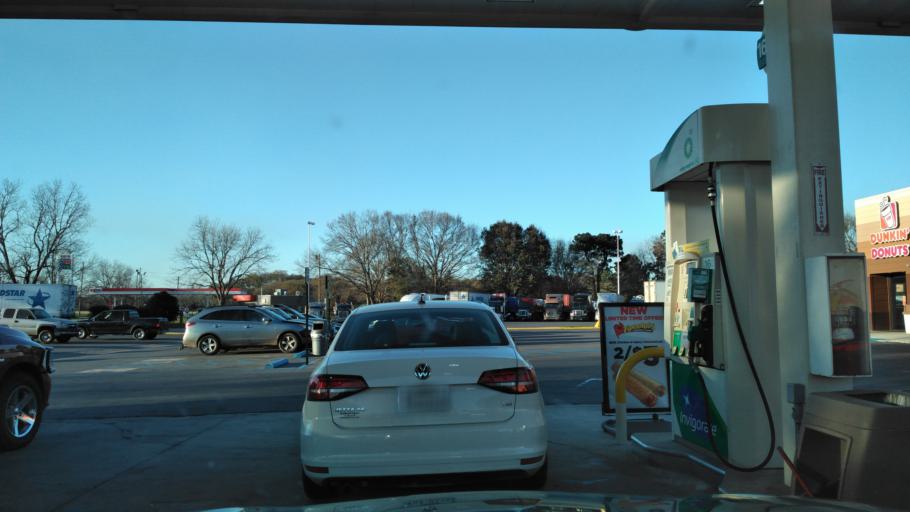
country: US
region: Alabama
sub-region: Mobile County
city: Grand Bay
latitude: 30.4984
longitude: -88.3339
